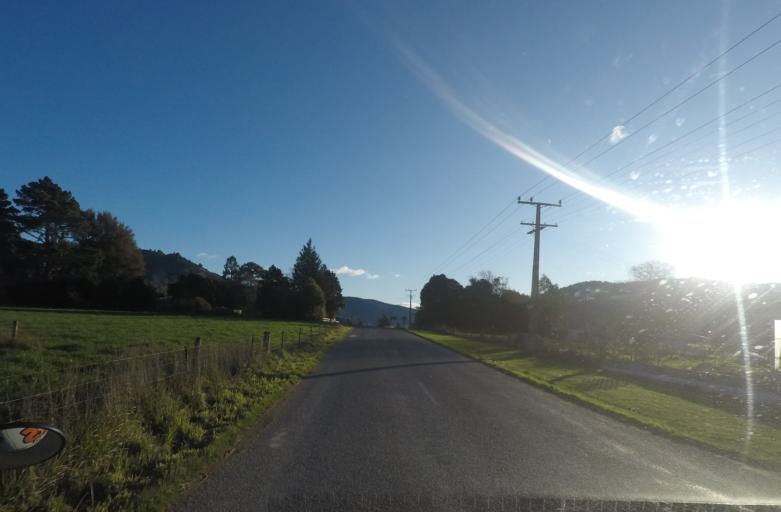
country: NZ
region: Marlborough
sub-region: Marlborough District
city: Picton
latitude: -41.2894
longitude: 173.8662
